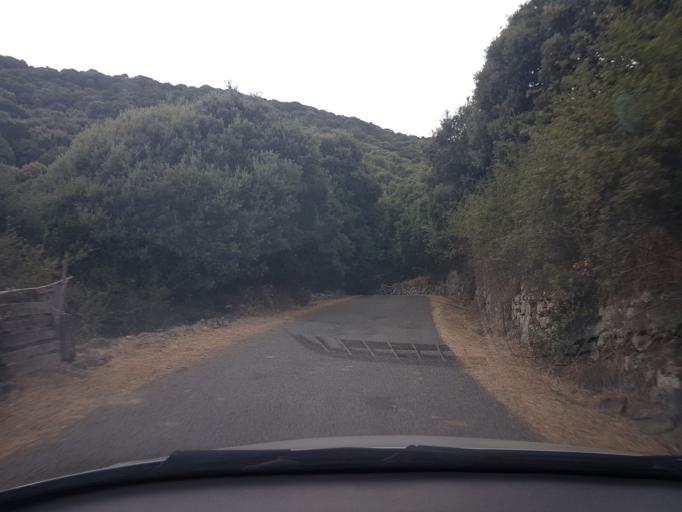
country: IT
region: Sardinia
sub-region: Provincia di Oristano
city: Seneghe
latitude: 40.1111
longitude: 8.6075
